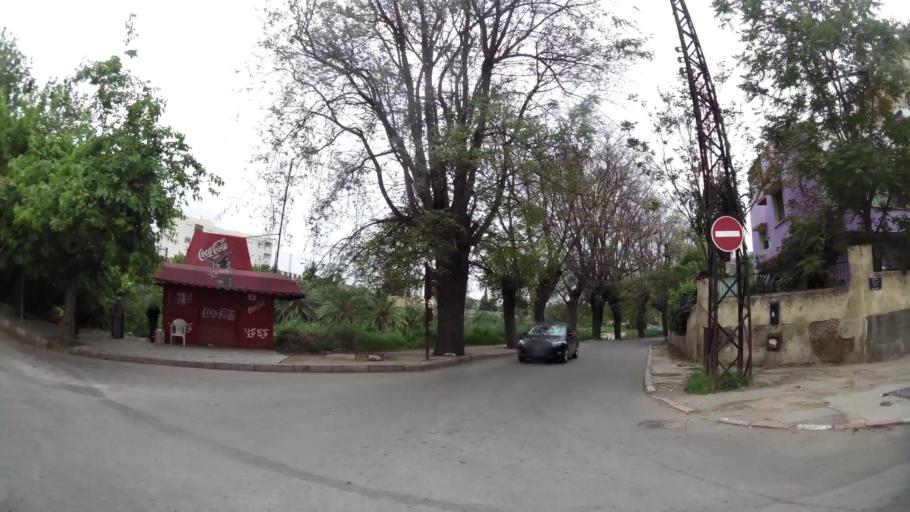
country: MA
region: Fes-Boulemane
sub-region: Fes
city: Fes
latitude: 34.0323
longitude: -4.9916
